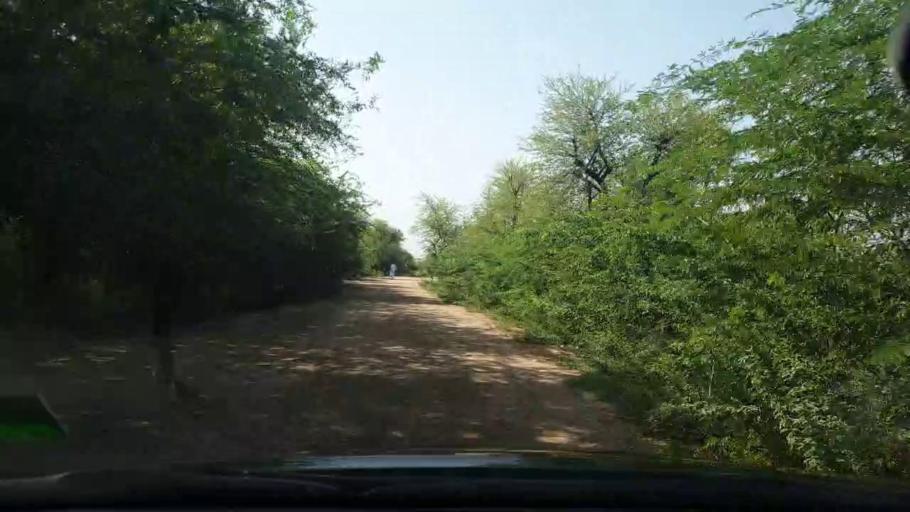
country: PK
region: Sindh
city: Tando Bago
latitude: 24.7473
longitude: 68.9865
